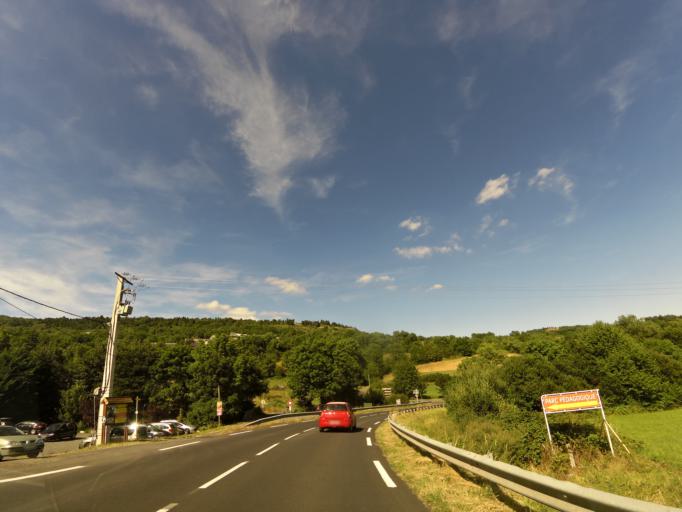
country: FR
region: Auvergne
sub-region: Departement du Puy-de-Dome
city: Aydat
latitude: 45.5890
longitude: 2.9627
